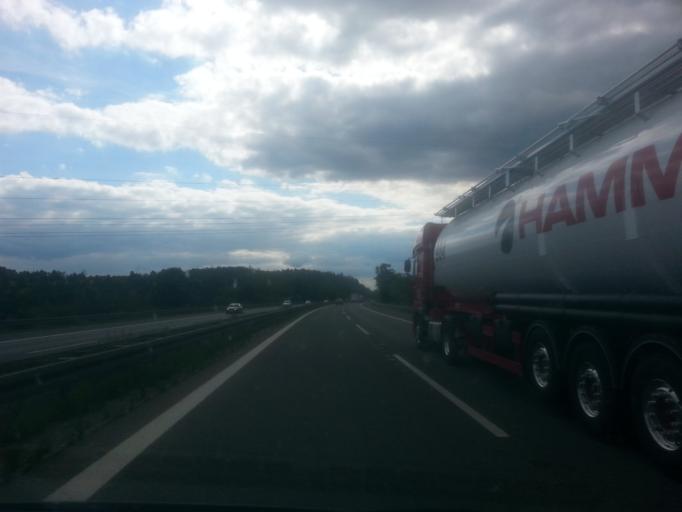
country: DE
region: Bavaria
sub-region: Upper Palatinate
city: Schwarzenfeld
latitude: 49.3977
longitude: 12.1588
